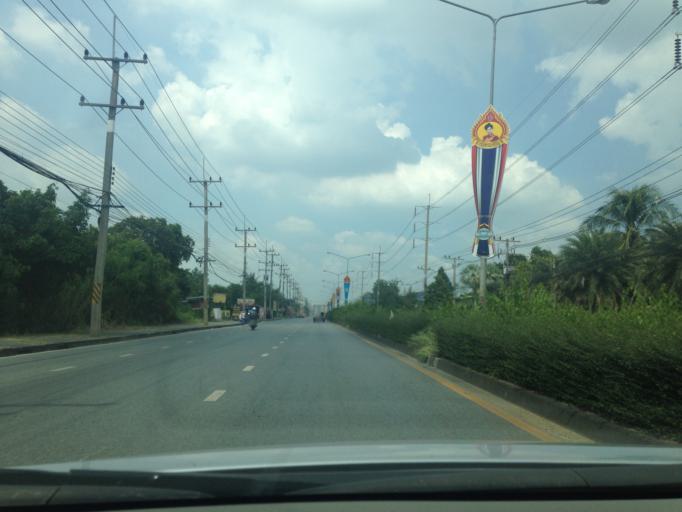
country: TH
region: Pathum Thani
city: Sam Khok
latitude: 14.0534
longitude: 100.5244
